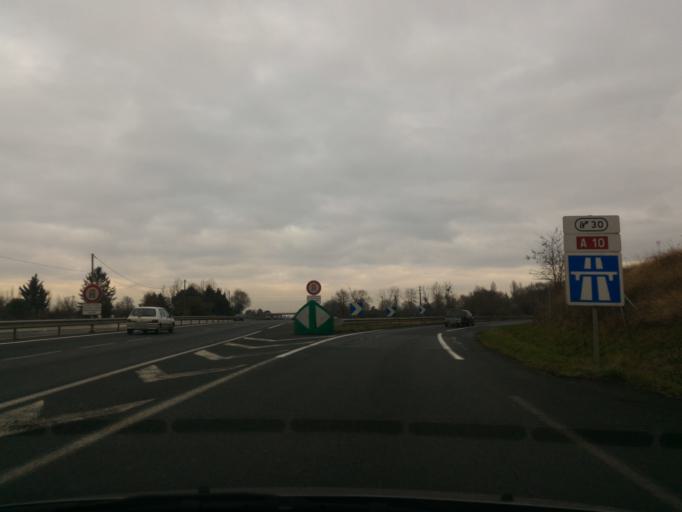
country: FR
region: Poitou-Charentes
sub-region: Departement de la Vienne
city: Fontaine-le-Comte
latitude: 46.5422
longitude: 0.2930
